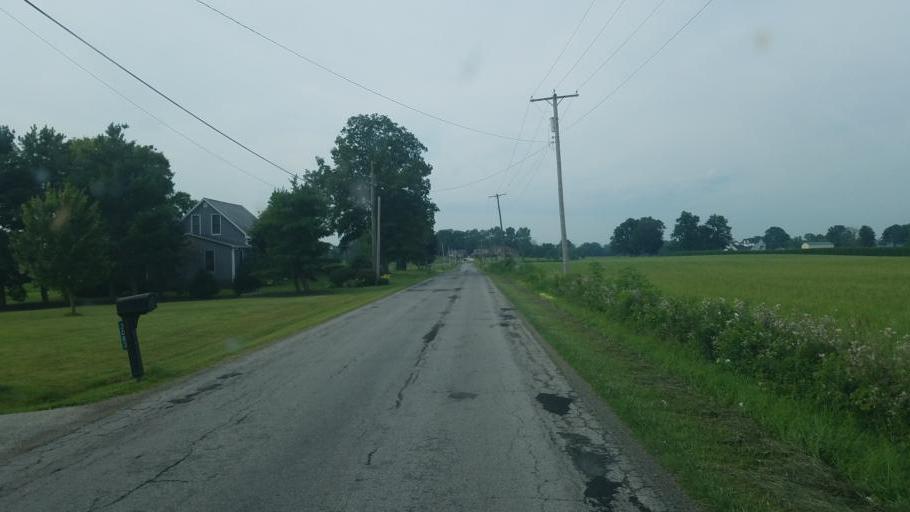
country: US
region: Ohio
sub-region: Morrow County
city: Cardington
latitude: 40.4707
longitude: -82.8961
